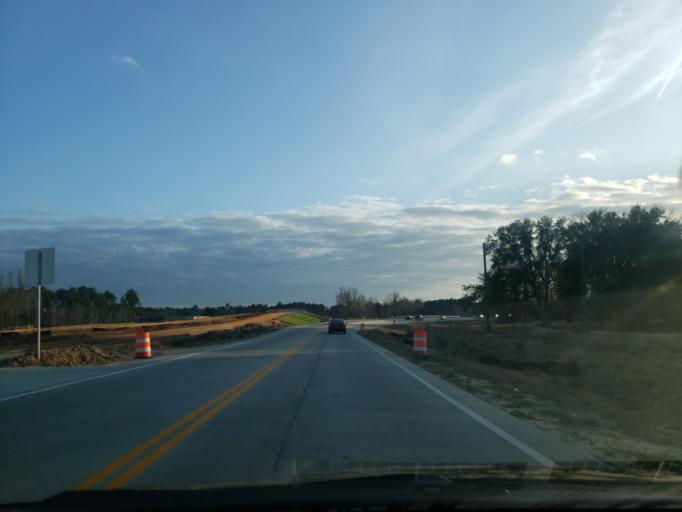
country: US
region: Georgia
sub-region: Chatham County
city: Bloomingdale
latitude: 32.1399
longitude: -81.3088
